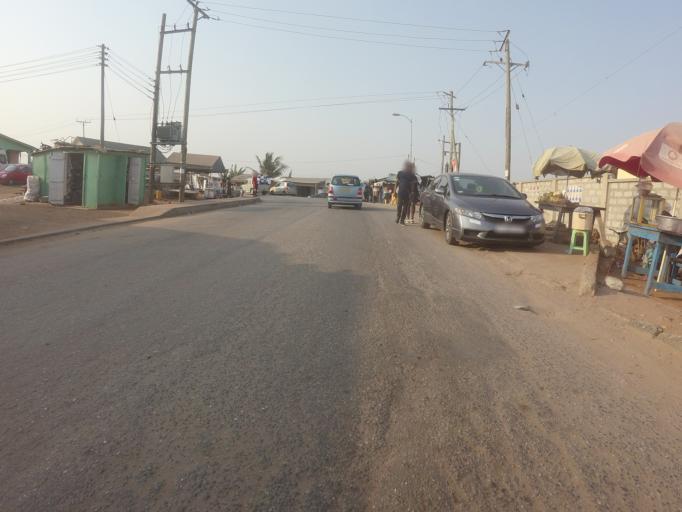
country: GH
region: Greater Accra
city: Nungua
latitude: 5.6138
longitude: -0.0470
